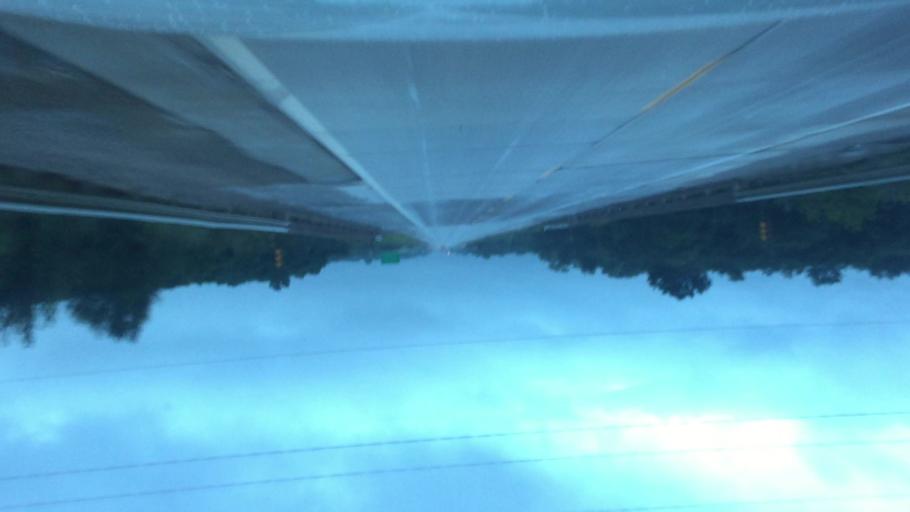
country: US
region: Kansas
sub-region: Neosho County
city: Chanute
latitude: 37.7040
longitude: -95.4795
